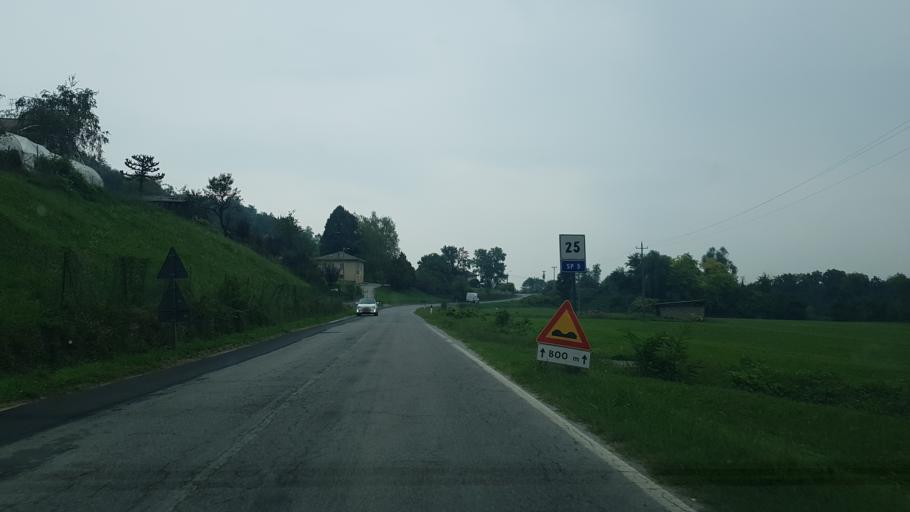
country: IT
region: Piedmont
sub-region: Provincia di Cuneo
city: Villanova Mondovi
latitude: 44.3349
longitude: 7.7580
